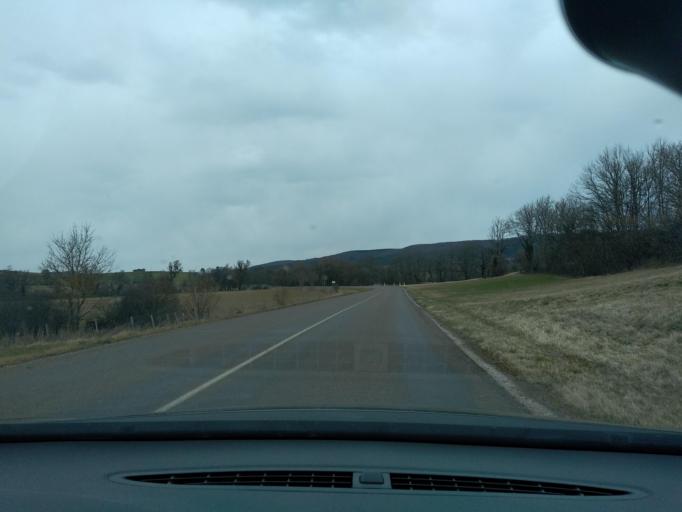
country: FR
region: Franche-Comte
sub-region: Departement du Jura
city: Arinthod
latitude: 46.4352
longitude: 5.5572
